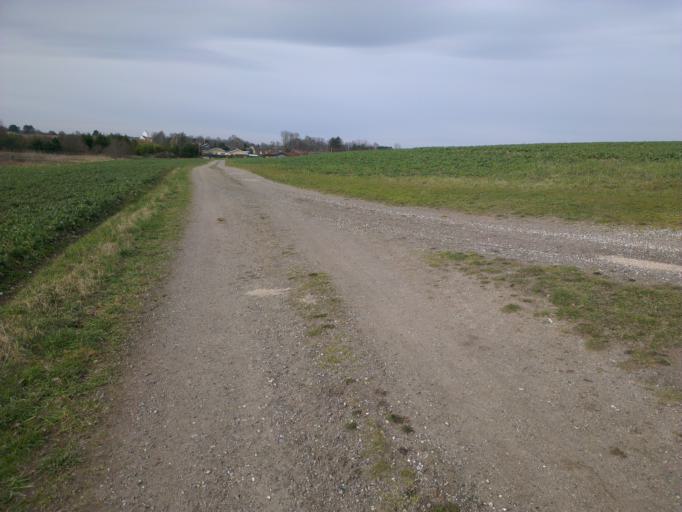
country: DK
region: Capital Region
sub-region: Frederikssund Kommune
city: Frederikssund
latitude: 55.8225
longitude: 12.0291
